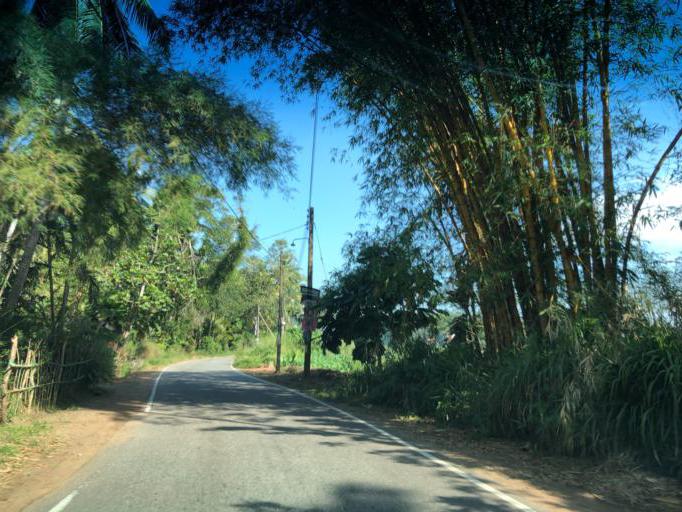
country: LK
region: Western
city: Homagama
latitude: 6.7981
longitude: 79.9820
